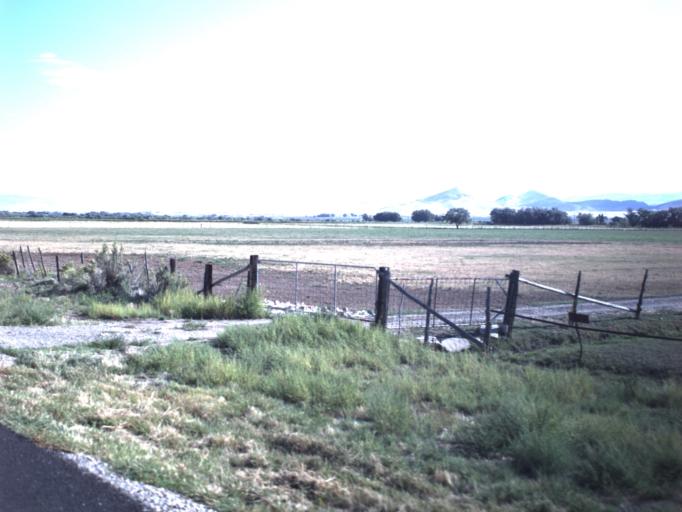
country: US
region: Utah
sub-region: Sevier County
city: Salina
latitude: 38.9778
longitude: -111.8605
